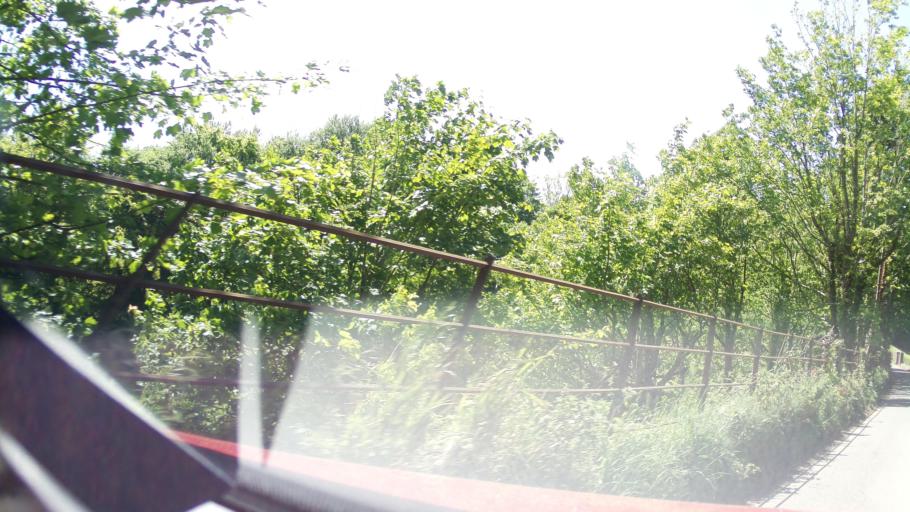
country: GB
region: England
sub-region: Devon
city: Budleigh Salterton
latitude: 50.6640
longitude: -3.3104
